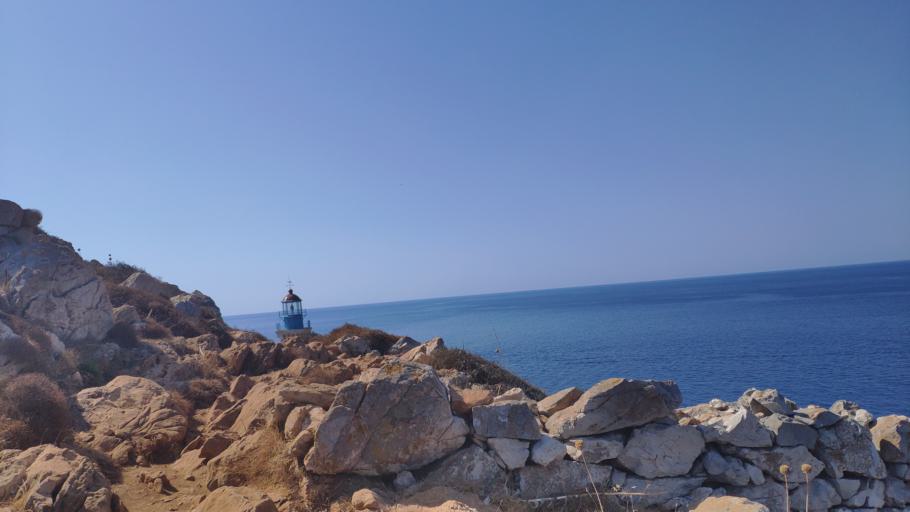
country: GR
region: Peloponnese
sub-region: Nomos Lakonias
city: Gytheio
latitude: 36.3870
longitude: 22.4827
